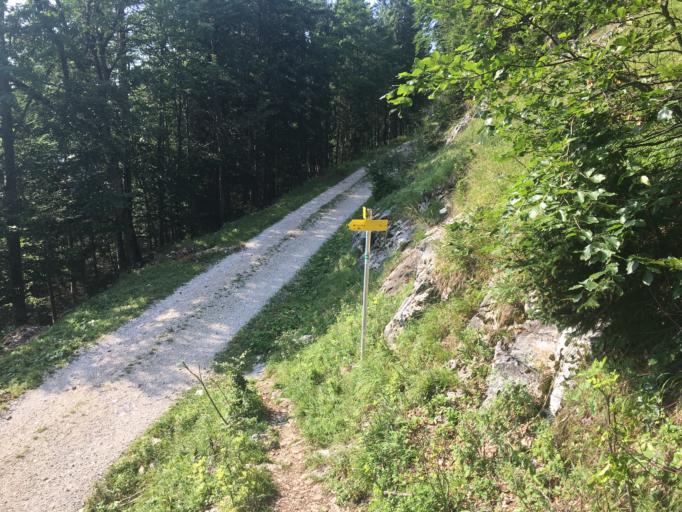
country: AT
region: Upper Austria
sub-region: Politischer Bezirk Gmunden
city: Sankt Wolfgang im Salzkammergut
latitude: 47.7762
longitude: 13.4190
